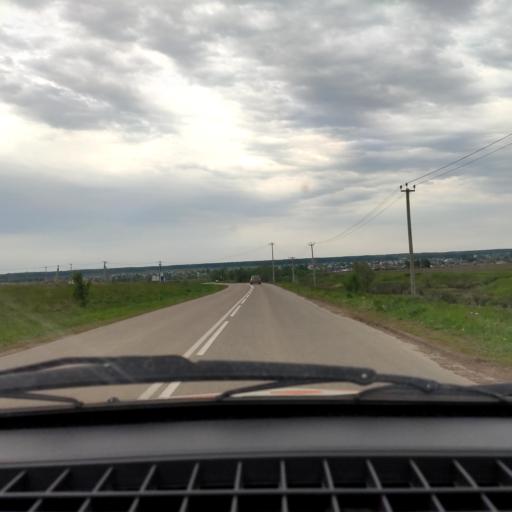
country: RU
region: Bashkortostan
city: Avdon
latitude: 54.5627
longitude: 55.7612
